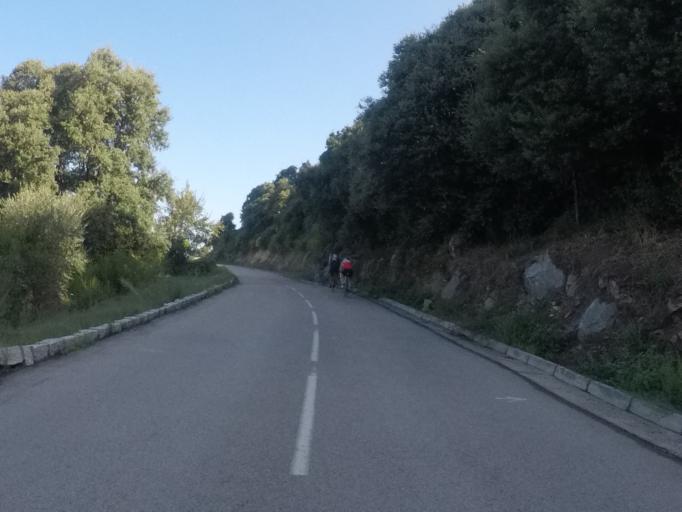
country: FR
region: Corsica
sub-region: Departement de la Corse-du-Sud
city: Olmeto
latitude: 41.7430
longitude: 8.8986
